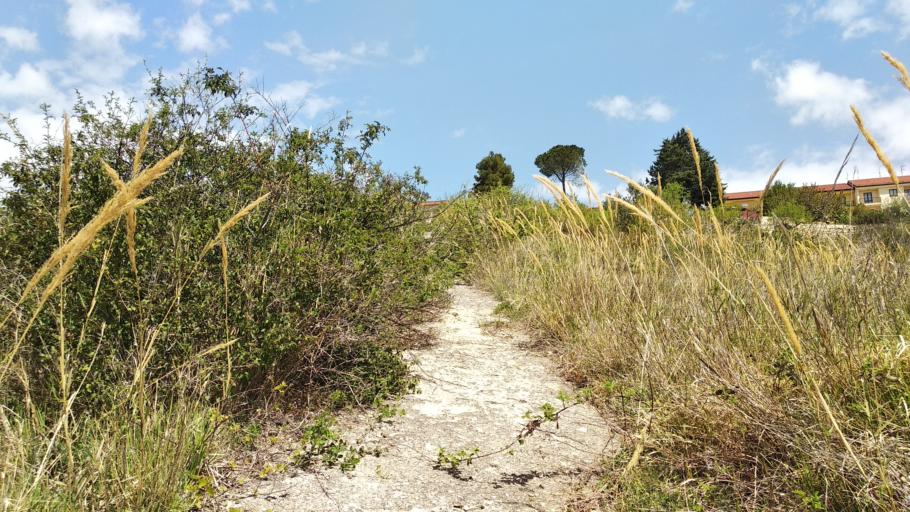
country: IT
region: Basilicate
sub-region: Provincia di Matera
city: Tricarico
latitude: 40.6135
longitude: 16.1408
